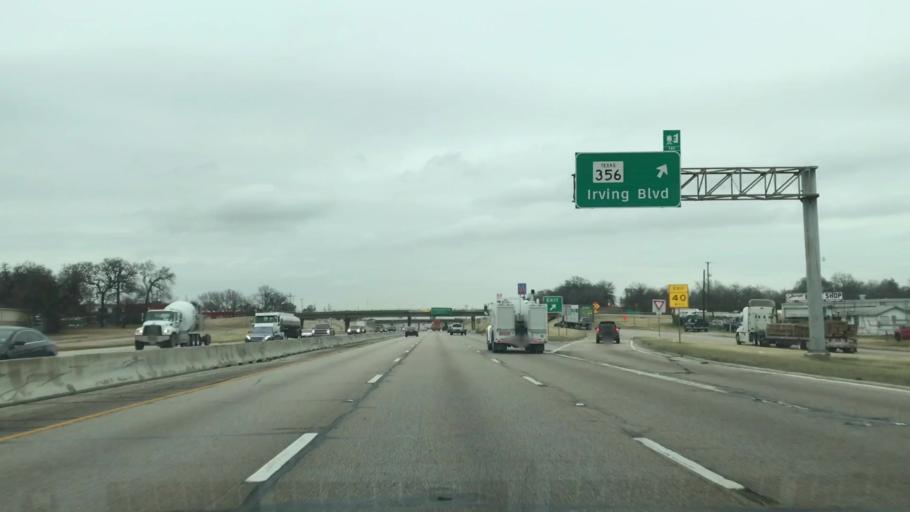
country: US
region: Texas
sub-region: Dallas County
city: Irving
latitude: 32.8044
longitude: -96.9216
